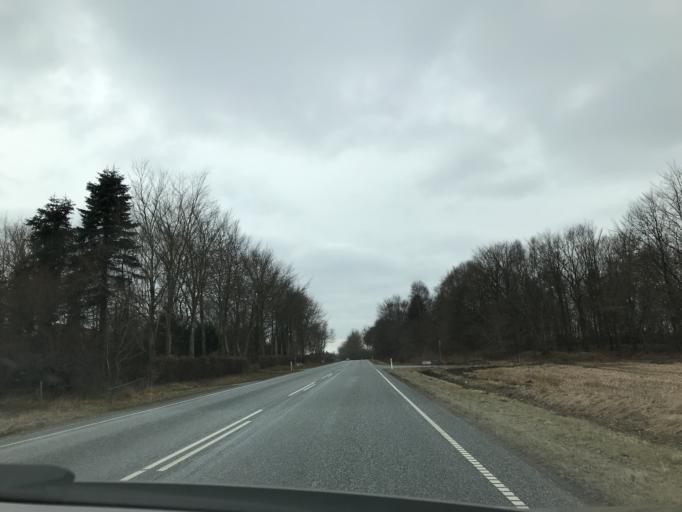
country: DK
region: South Denmark
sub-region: Varde Kommune
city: Olgod
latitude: 55.8437
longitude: 8.7110
